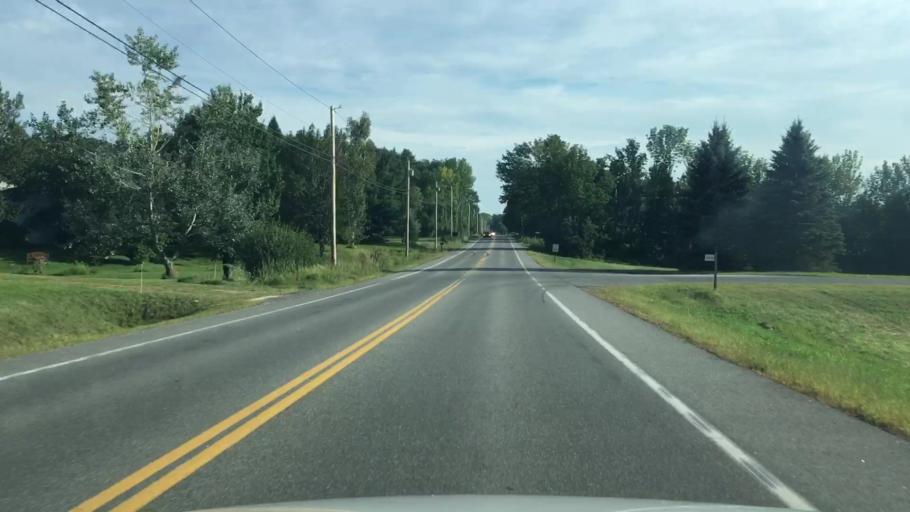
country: US
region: Maine
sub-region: Cumberland County
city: North Windham
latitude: 43.7854
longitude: -70.4397
